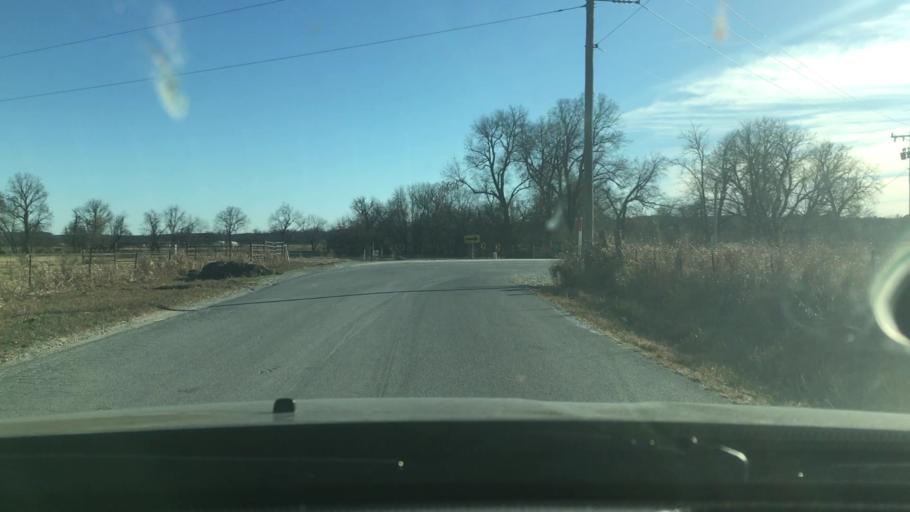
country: US
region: Oklahoma
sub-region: Murray County
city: Davis
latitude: 34.4999
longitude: -97.1559
